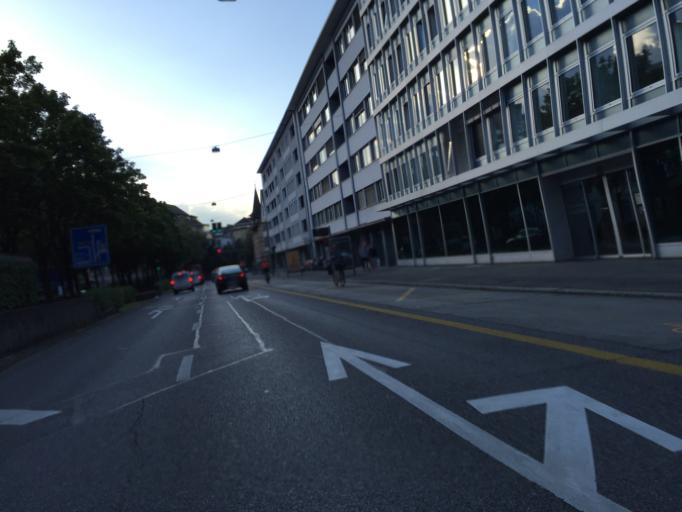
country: CH
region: Bern
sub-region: Bern-Mittelland District
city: Bern
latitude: 46.9446
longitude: 7.4305
